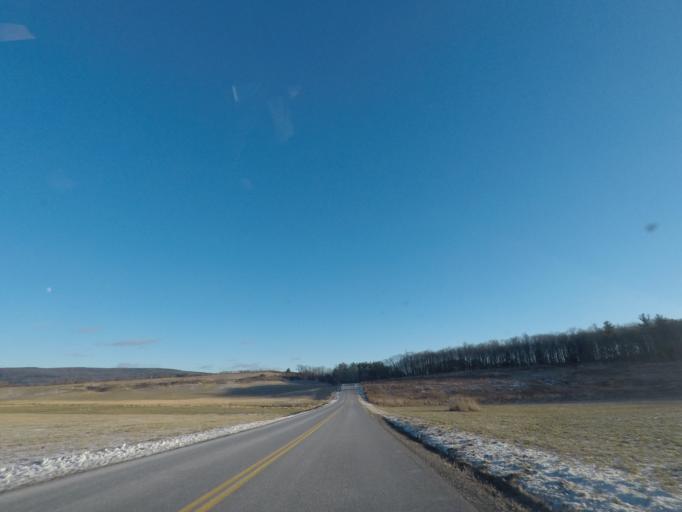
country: US
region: New York
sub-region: Rensselaer County
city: Poestenkill
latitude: 42.7138
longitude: -73.5916
